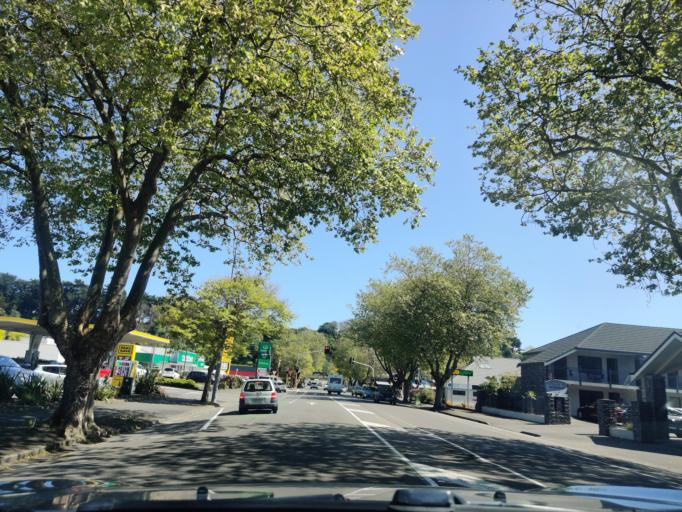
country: NZ
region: Manawatu-Wanganui
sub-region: Wanganui District
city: Wanganui
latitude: -39.9260
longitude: 175.0404
